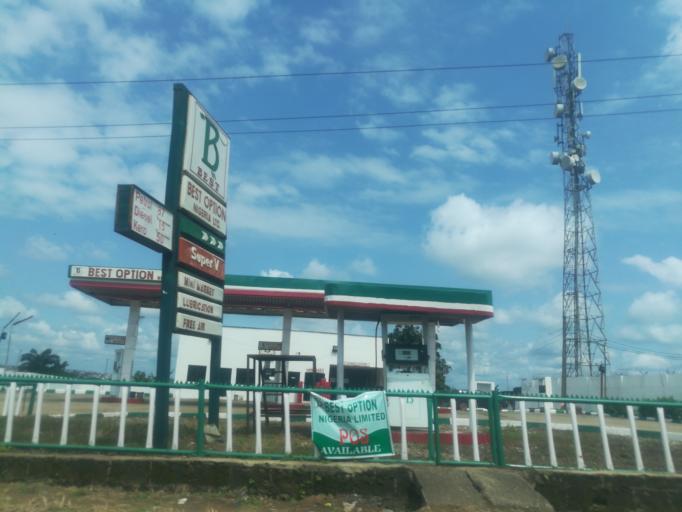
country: NG
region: Oyo
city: Egbeda
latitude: 7.4270
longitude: 3.9964
